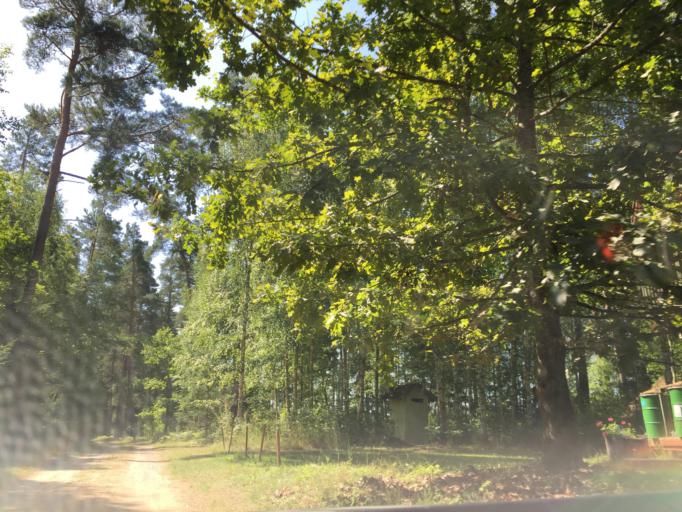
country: LV
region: Talsu Rajons
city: Stende
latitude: 57.1608
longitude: 22.3039
